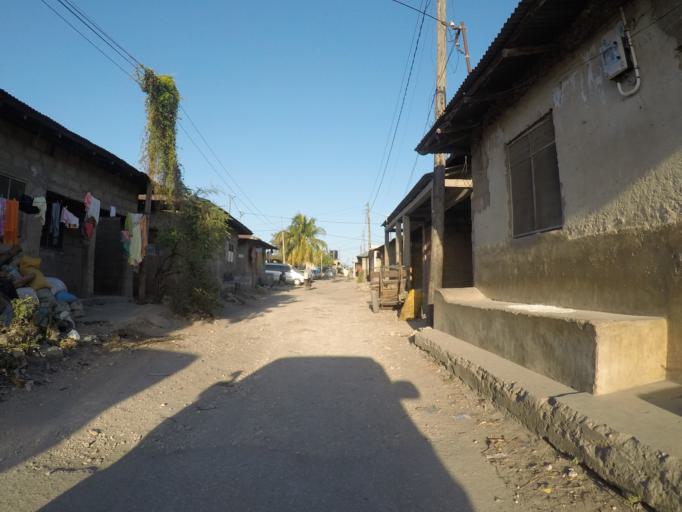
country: TZ
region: Zanzibar Urban/West
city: Zanzibar
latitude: -6.1579
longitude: 39.2130
